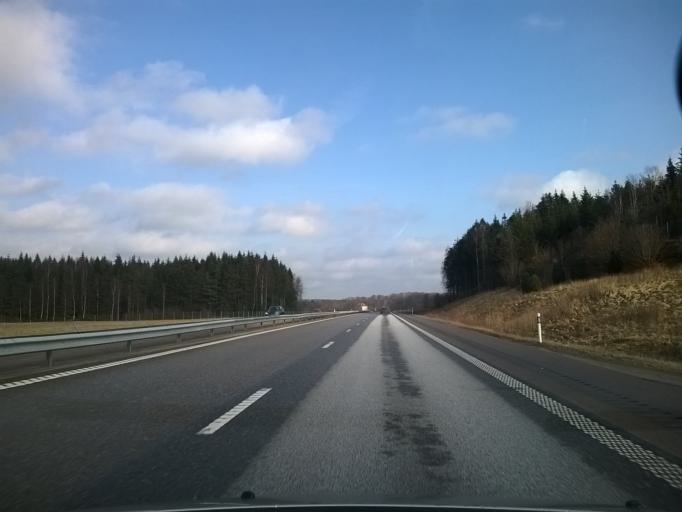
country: SE
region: Vaestra Goetaland
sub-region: Uddevalla Kommun
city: Uddevalla
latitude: 58.3089
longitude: 11.8591
